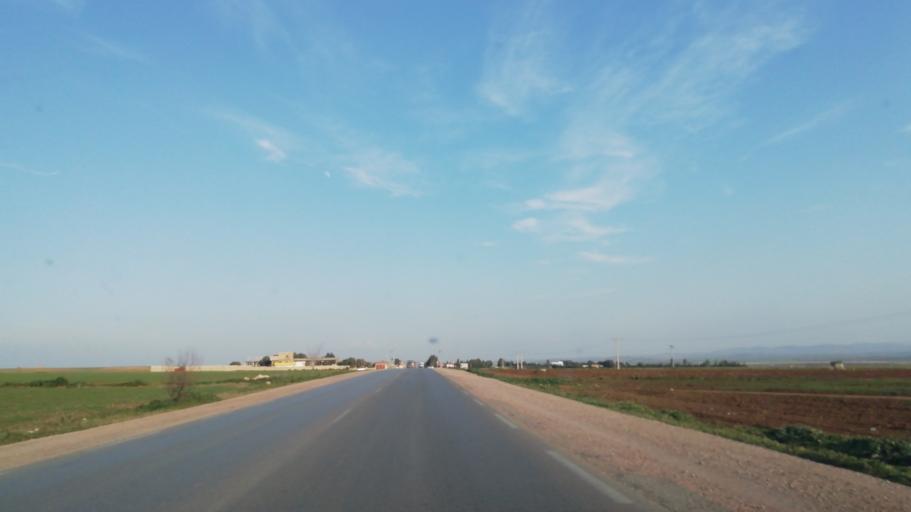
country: DZ
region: Relizane
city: Djidiouia
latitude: 35.8945
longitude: 0.6560
